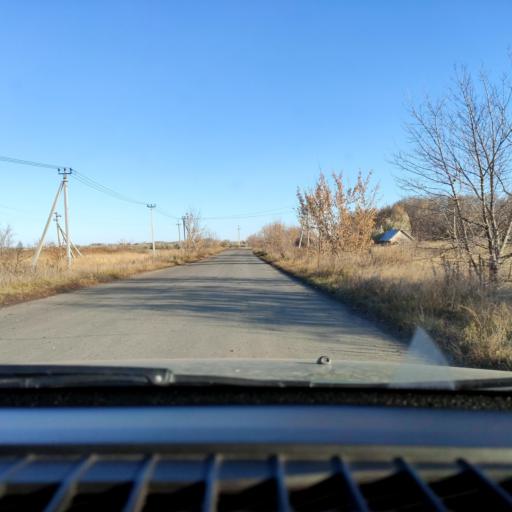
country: RU
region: Samara
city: Tol'yatti
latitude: 53.6475
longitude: 49.3197
